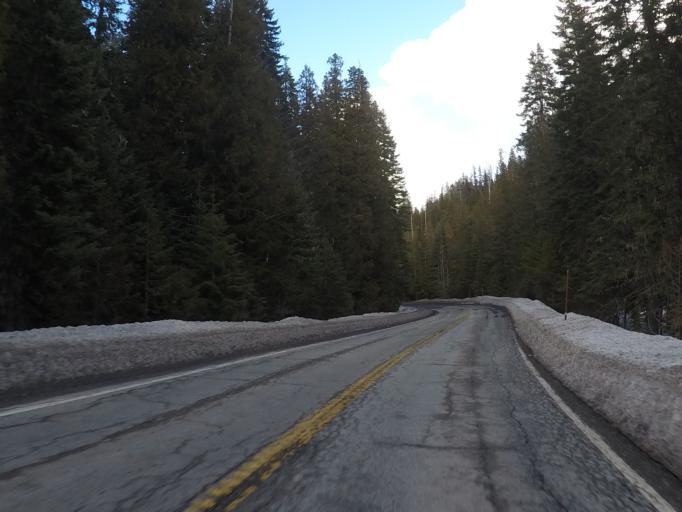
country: US
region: Montana
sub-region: Ravalli County
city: Stevensville
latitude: 46.5580
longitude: -114.6615
